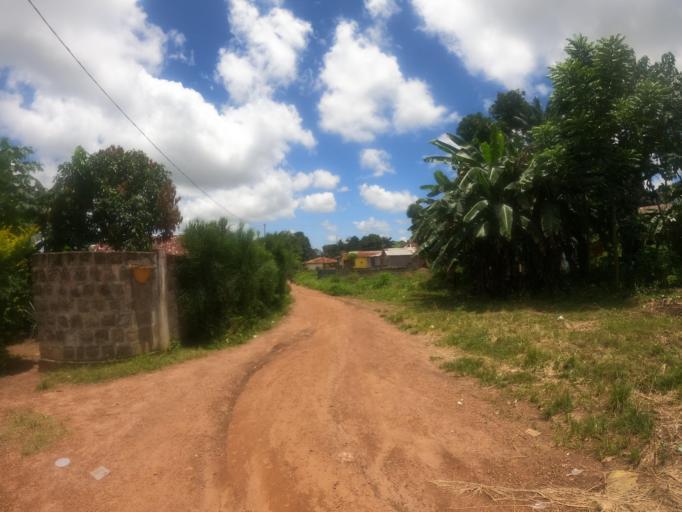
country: SL
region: Northern Province
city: Makeni
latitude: 8.8861
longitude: -12.0739
